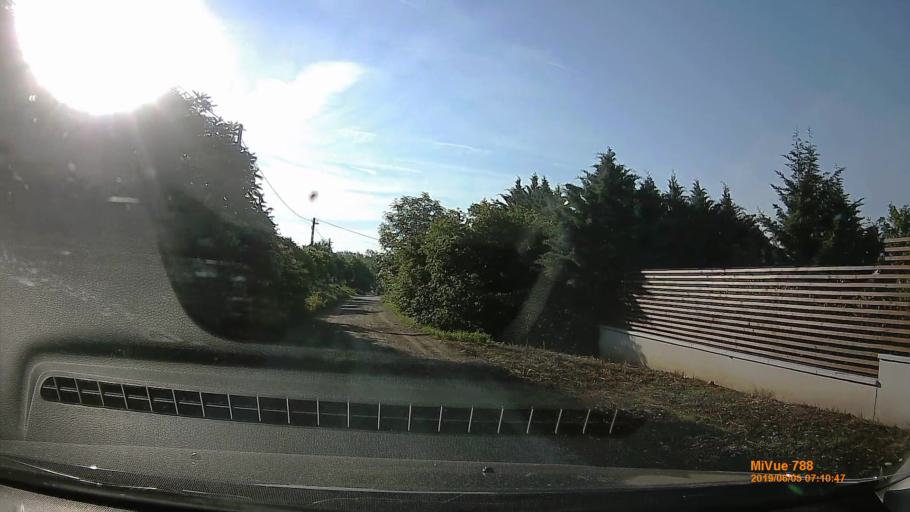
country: HU
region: Pest
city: Urom
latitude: 47.5836
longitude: 19.0294
